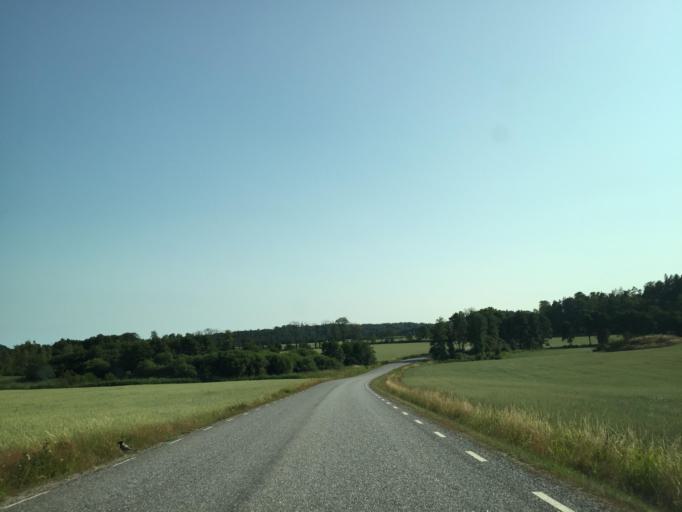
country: SE
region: Vaestra Goetaland
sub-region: Lilla Edets Kommun
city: Lilla Edet
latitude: 58.2014
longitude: 12.1230
